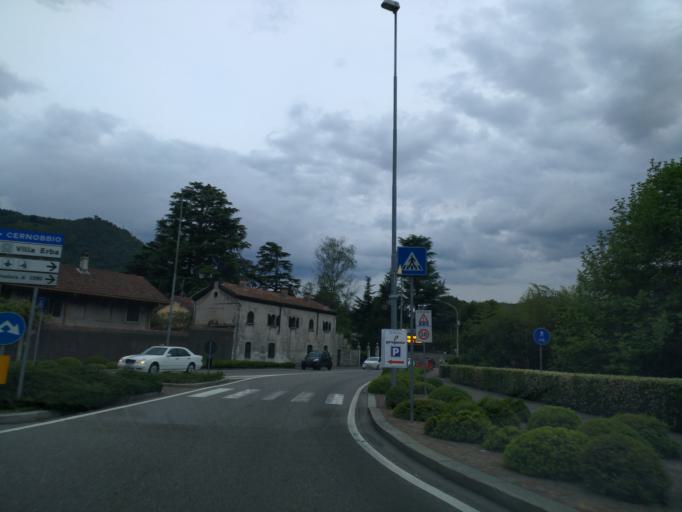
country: IT
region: Lombardy
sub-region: Provincia di Como
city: Cernobbio
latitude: 45.8345
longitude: 9.0724
